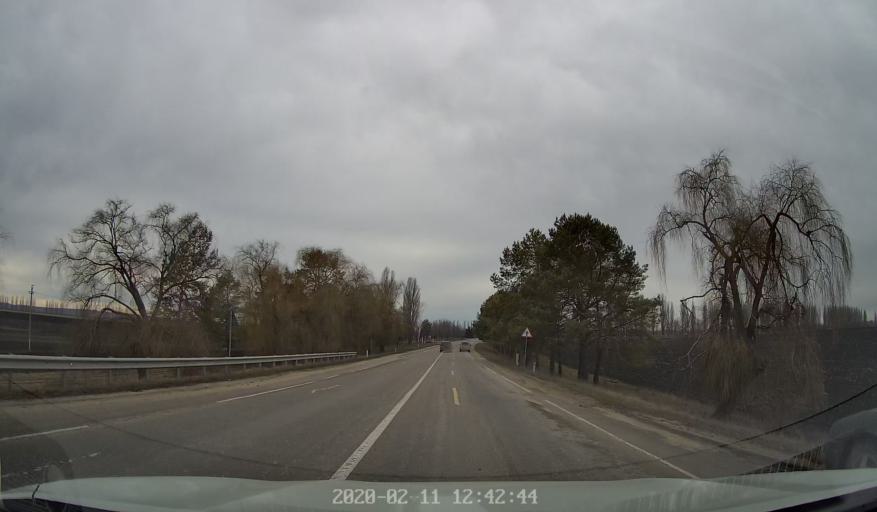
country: MD
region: Raionul Edinet
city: Edinet
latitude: 48.2256
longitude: 27.2181
